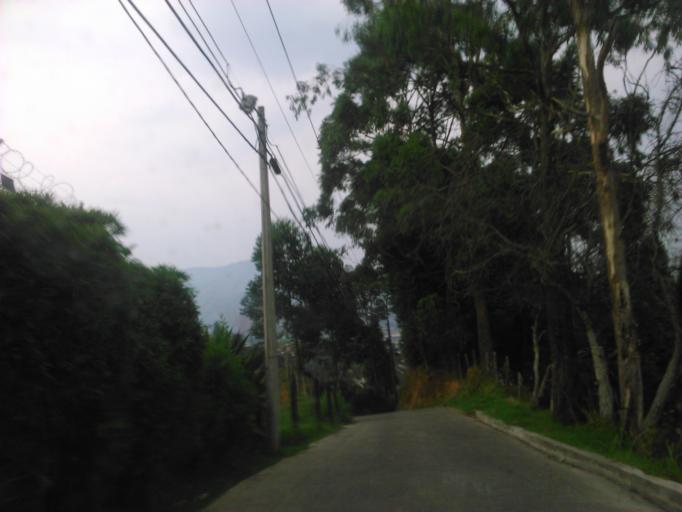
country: CO
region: Antioquia
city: La Estrella
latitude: 6.1408
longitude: -75.6386
